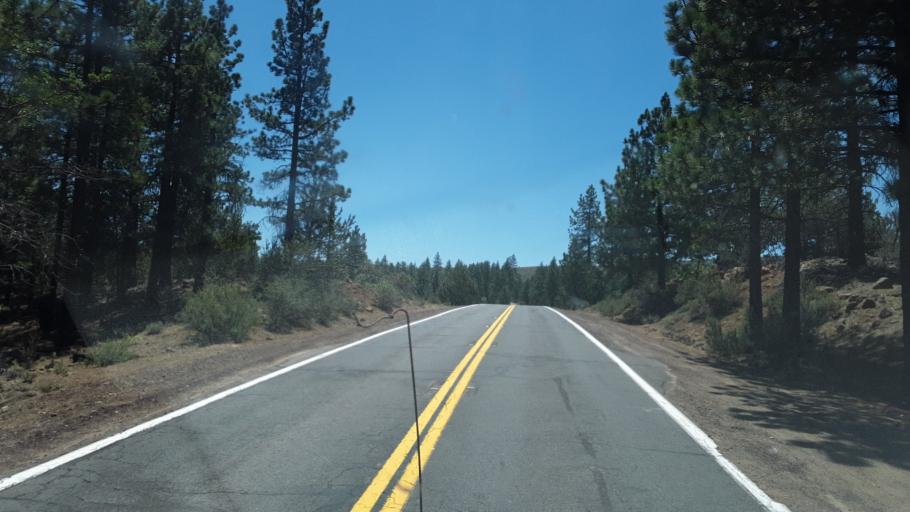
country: US
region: California
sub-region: Lassen County
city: Johnstonville
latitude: 40.4756
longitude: -120.5547
